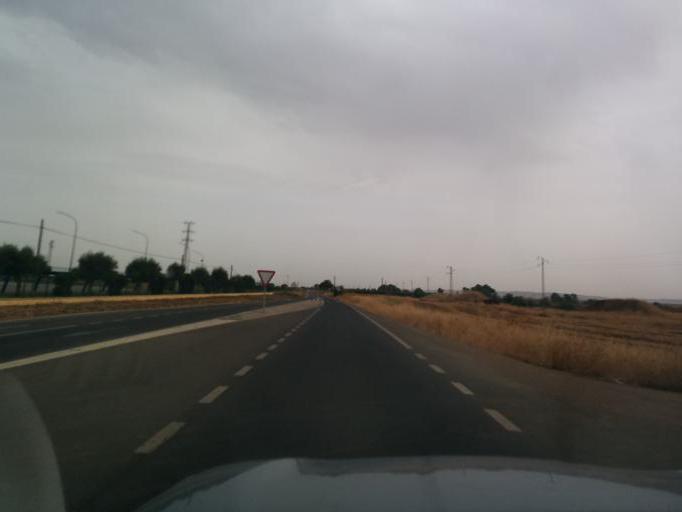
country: ES
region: Andalusia
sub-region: Provincia de Sevilla
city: Guillena
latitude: 37.5375
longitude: -6.0354
